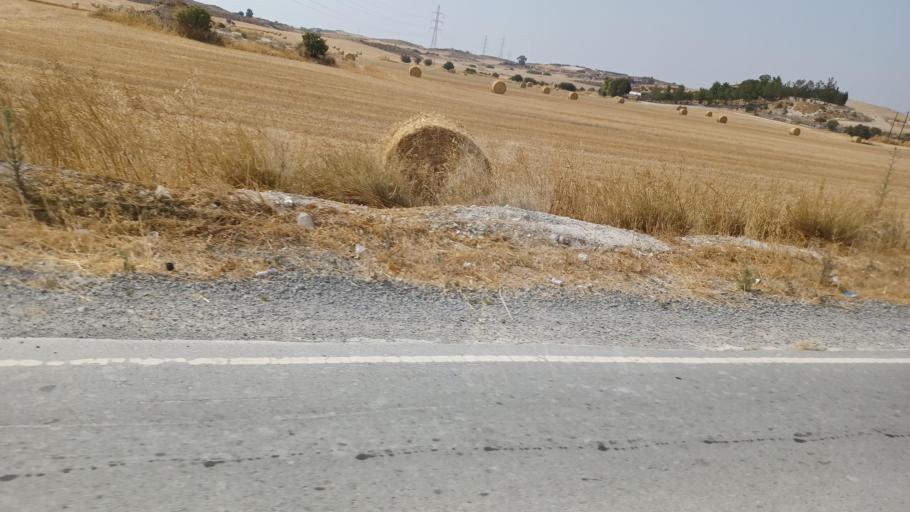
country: CY
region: Larnaka
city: Aradippou
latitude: 34.9373
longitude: 33.5504
